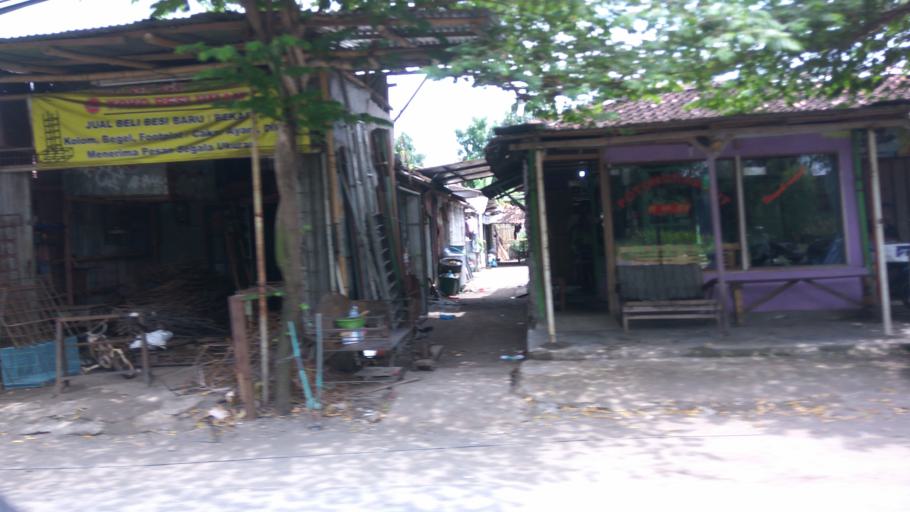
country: ID
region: Daerah Istimewa Yogyakarta
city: Depok
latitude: -7.7463
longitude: 110.4185
